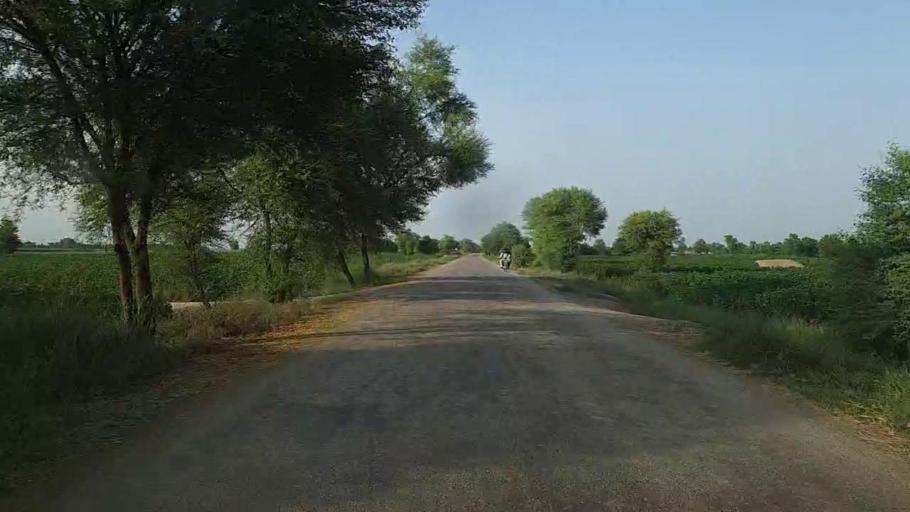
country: PK
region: Sindh
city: Ubauro
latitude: 28.1105
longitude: 69.8185
